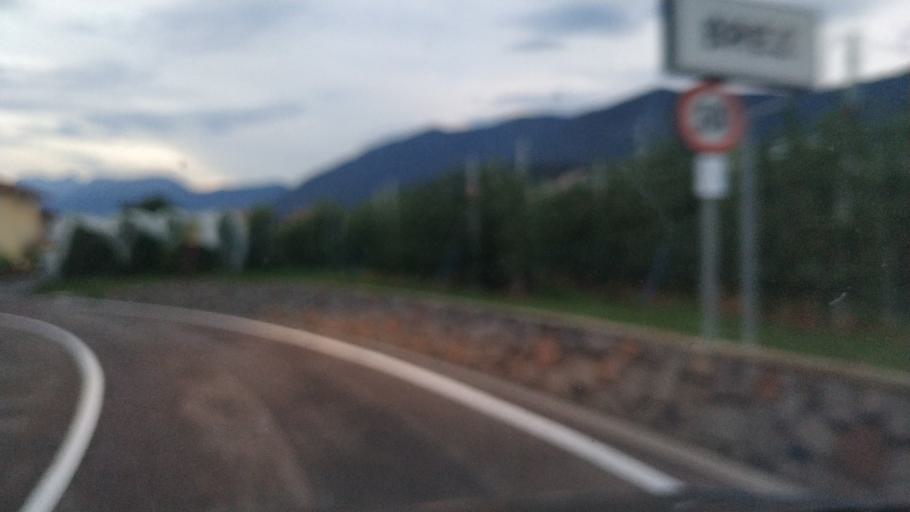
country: IT
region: Trentino-Alto Adige
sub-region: Provincia di Trento
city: Brez
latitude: 46.4341
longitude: 11.1086
